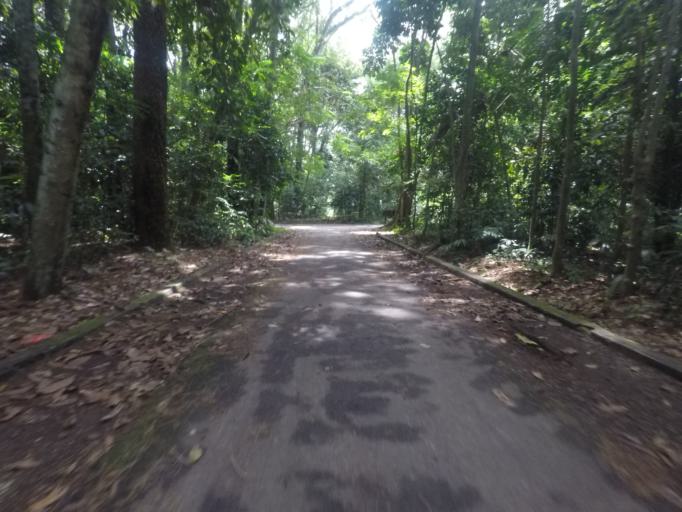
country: ID
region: West Java
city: Ciampea
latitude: -6.5511
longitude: 106.7499
